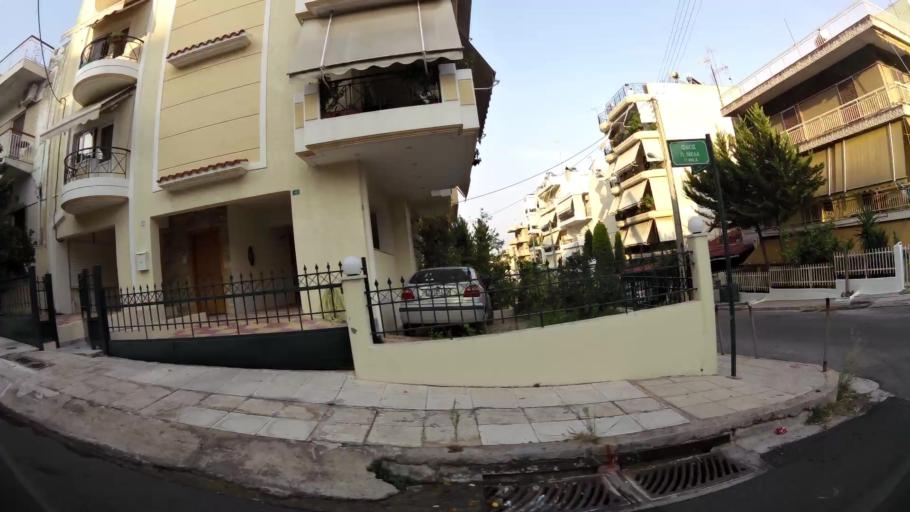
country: GR
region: Attica
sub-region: Nomarchia Athinas
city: Petroupolis
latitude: 38.0377
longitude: 23.6682
